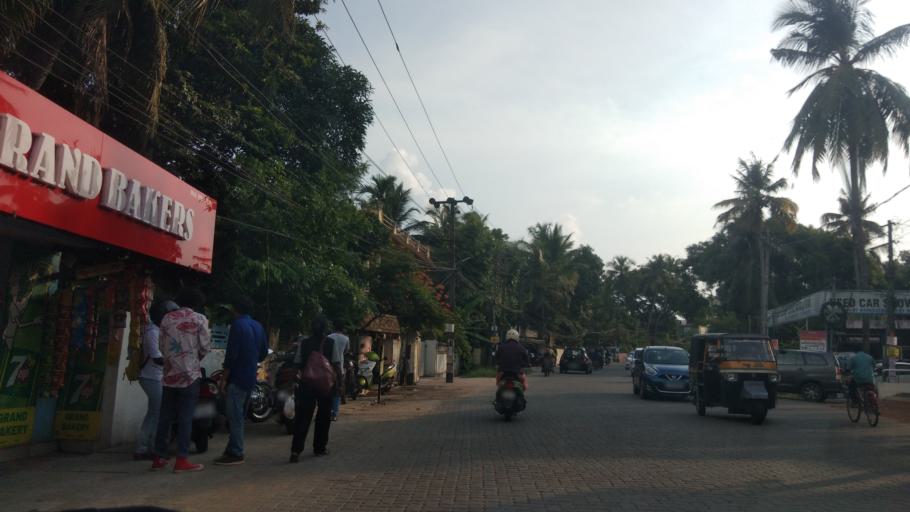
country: IN
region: Kerala
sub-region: Ernakulam
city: Cochin
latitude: 9.9396
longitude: 76.3309
